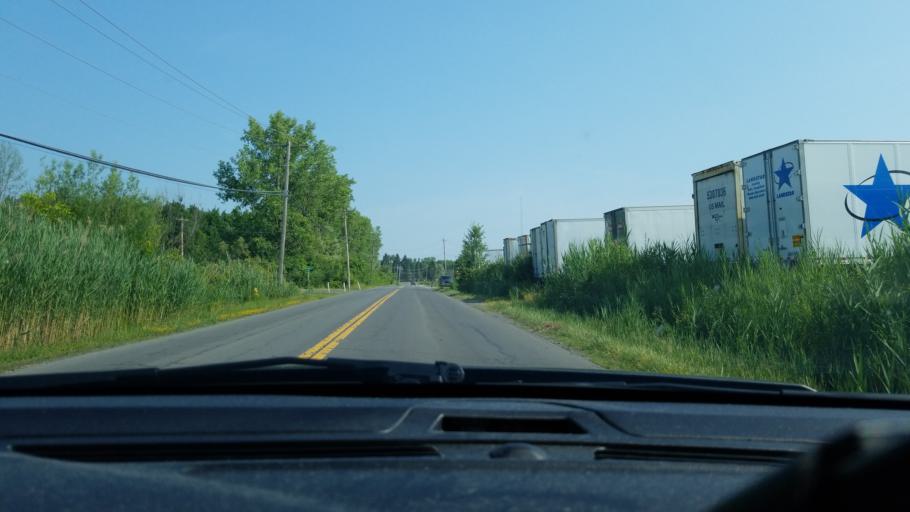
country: US
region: New York
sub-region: Onondaga County
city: North Syracuse
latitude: 43.1231
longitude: -76.0732
